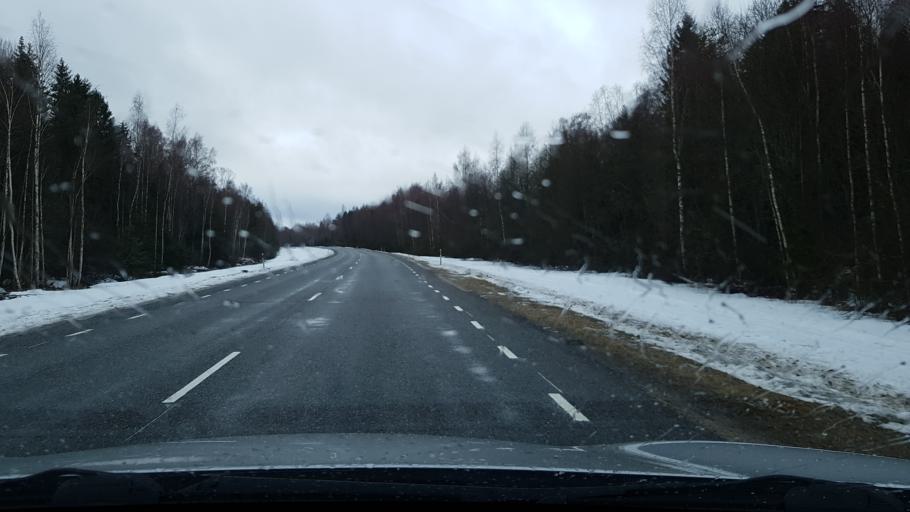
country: LV
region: Apes Novads
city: Ape
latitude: 57.6405
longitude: 26.6451
